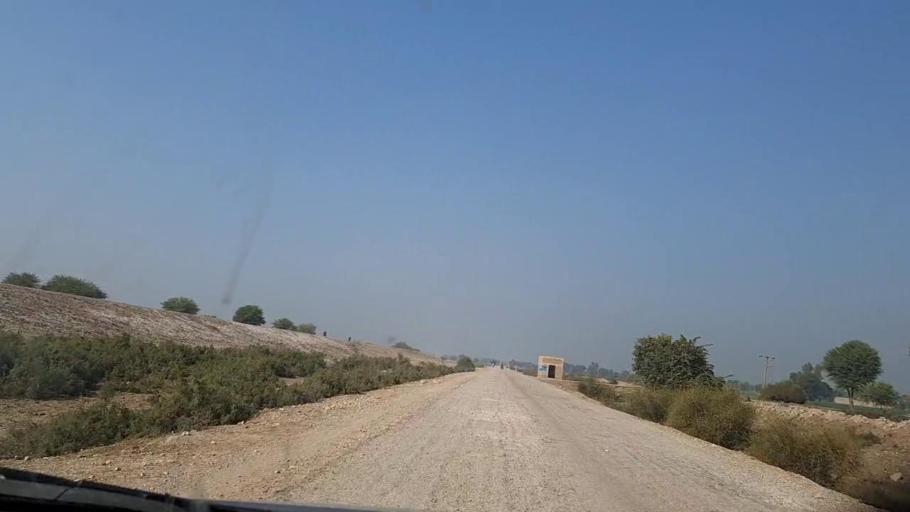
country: PK
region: Sindh
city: Moro
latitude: 26.7231
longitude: 67.9223
